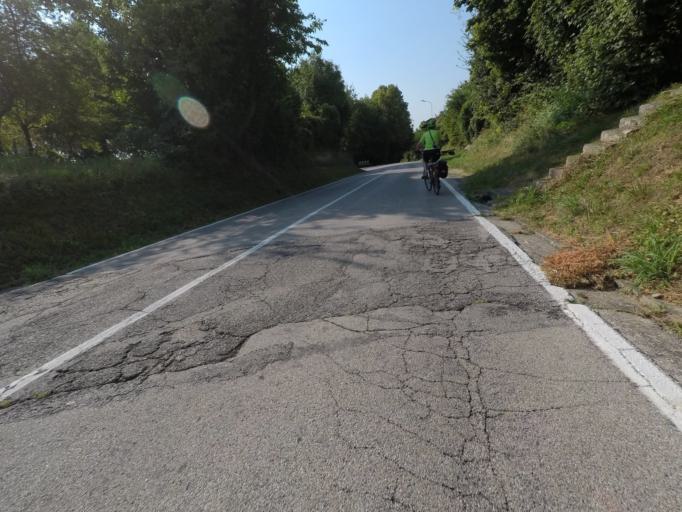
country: IT
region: Friuli Venezia Giulia
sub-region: Provincia di Pordenone
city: Pinzano al Tagliamento
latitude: 46.1827
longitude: 12.9510
